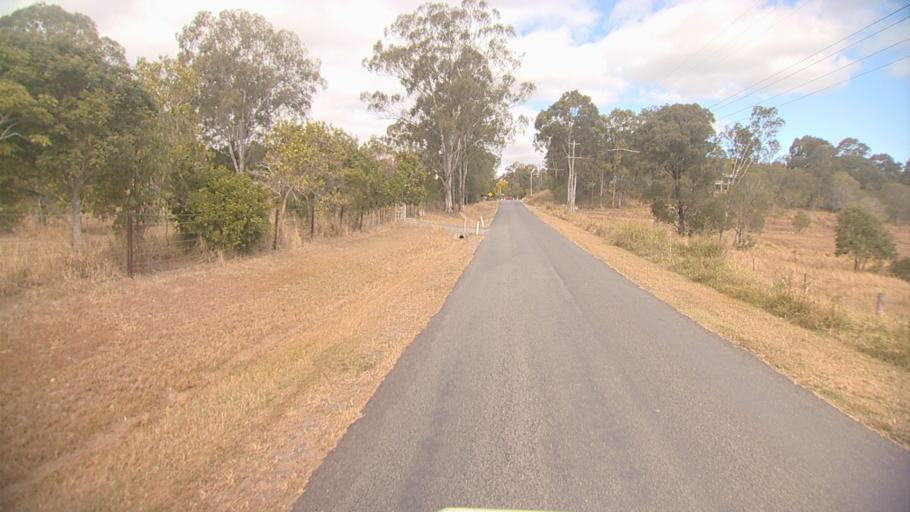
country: AU
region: Queensland
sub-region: Logan
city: Cedar Vale
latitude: -27.8803
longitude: 153.0278
